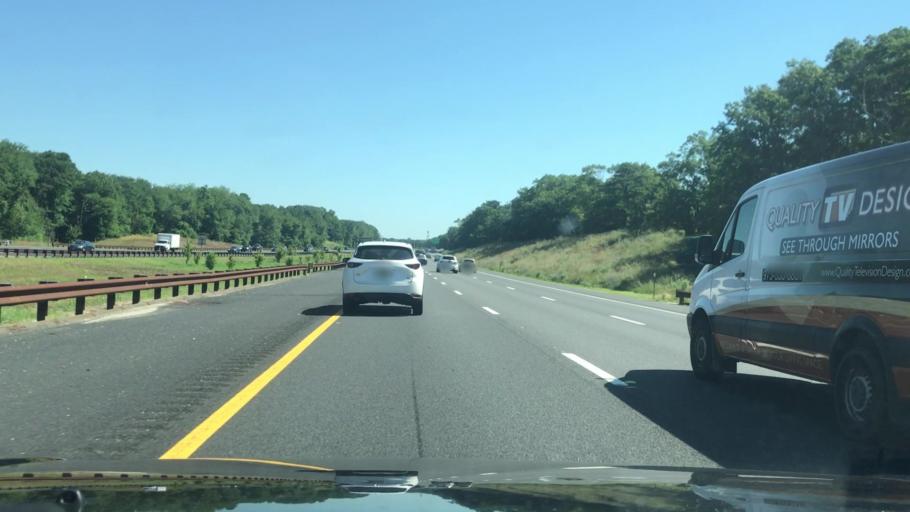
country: US
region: New Jersey
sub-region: Monmouth County
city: Ramtown
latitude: 40.0844
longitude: -74.1522
